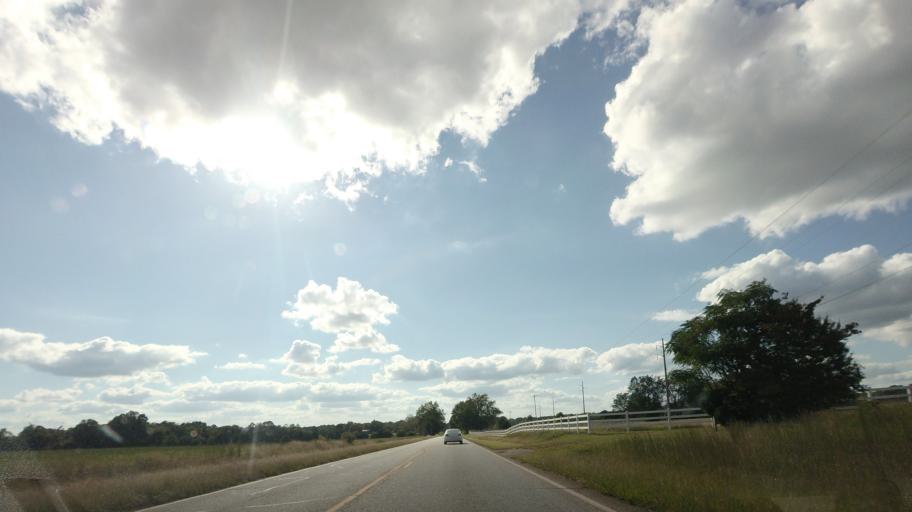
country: US
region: Georgia
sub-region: Lamar County
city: Barnesville
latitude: 33.0543
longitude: -84.0941
